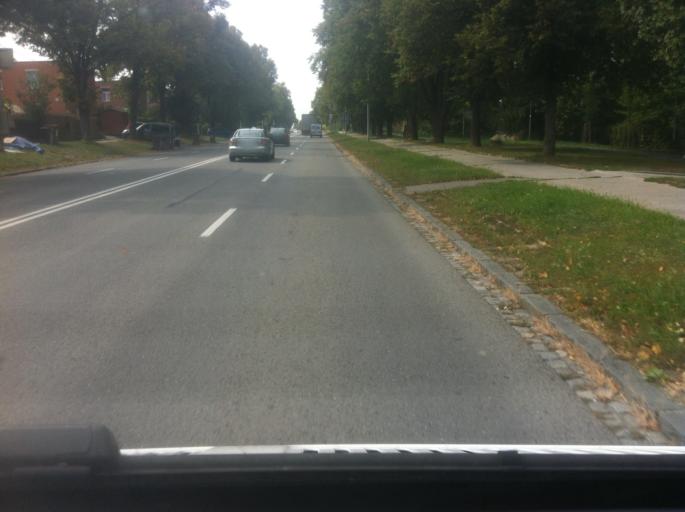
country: CZ
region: Zlin
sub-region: Okres Zlin
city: Zlin
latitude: 49.2253
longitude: 17.6879
